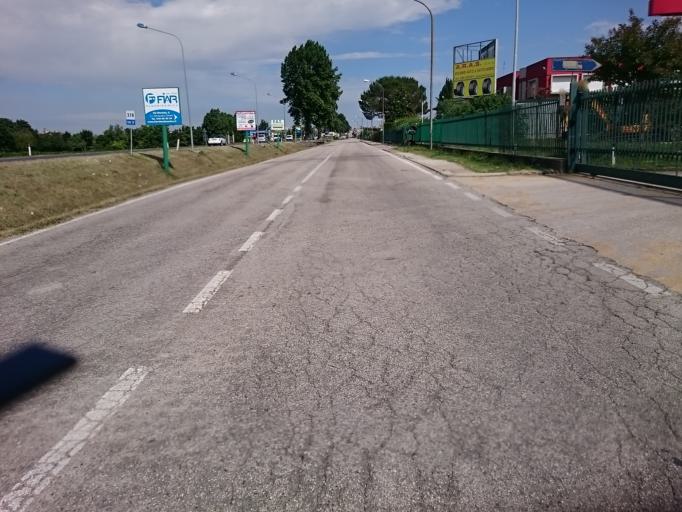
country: IT
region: Veneto
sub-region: Provincia di Padova
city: Rubano
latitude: 45.4228
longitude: 11.8000
